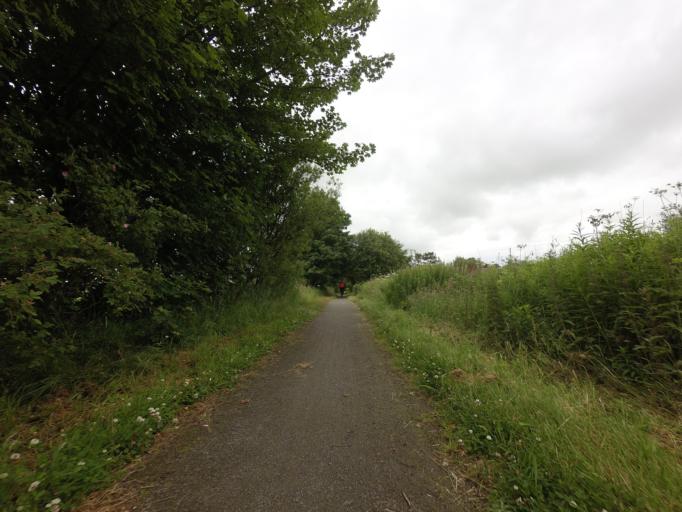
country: GB
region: Scotland
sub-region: Aberdeenshire
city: Ellon
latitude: 57.4680
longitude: -2.1185
